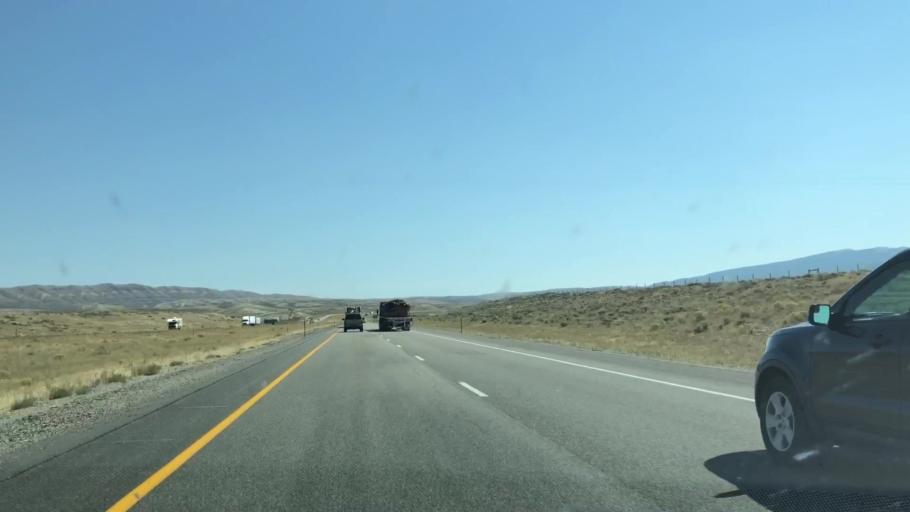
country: US
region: Wyoming
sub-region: Carbon County
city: Saratoga
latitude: 41.7419
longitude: -106.7918
